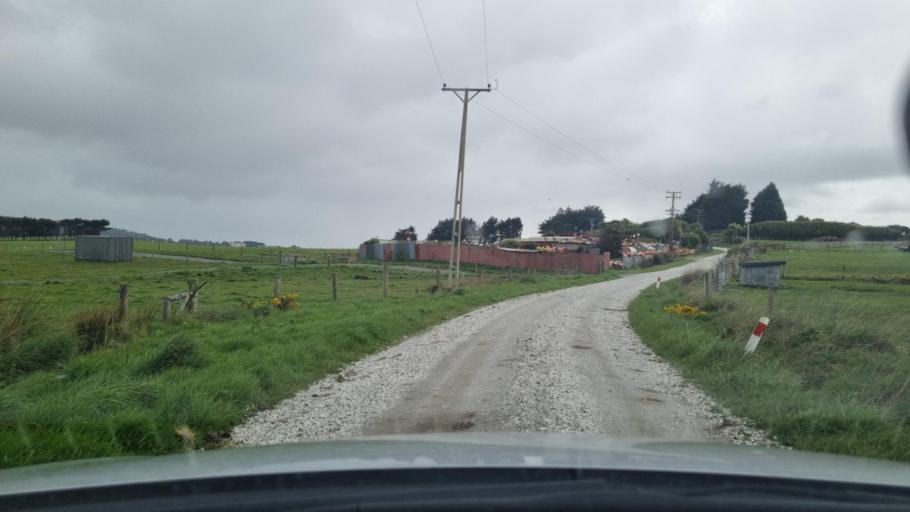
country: NZ
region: Southland
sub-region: Invercargill City
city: Bluff
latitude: -46.5403
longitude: 168.2906
